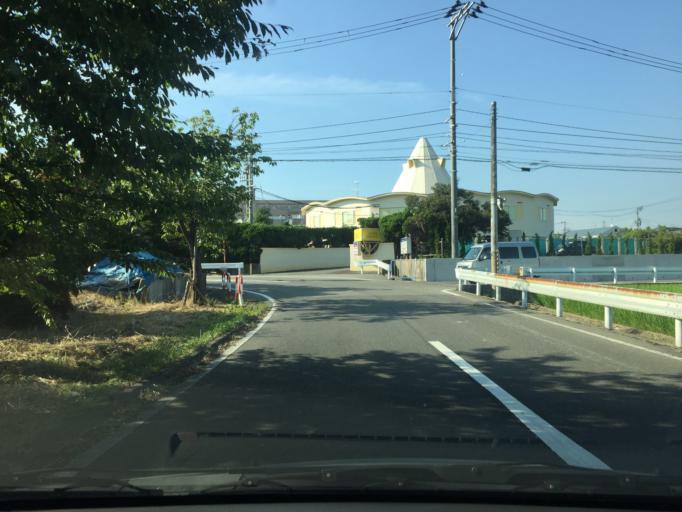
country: JP
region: Niigata
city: Niigata-shi
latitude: 37.8948
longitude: 139.0556
